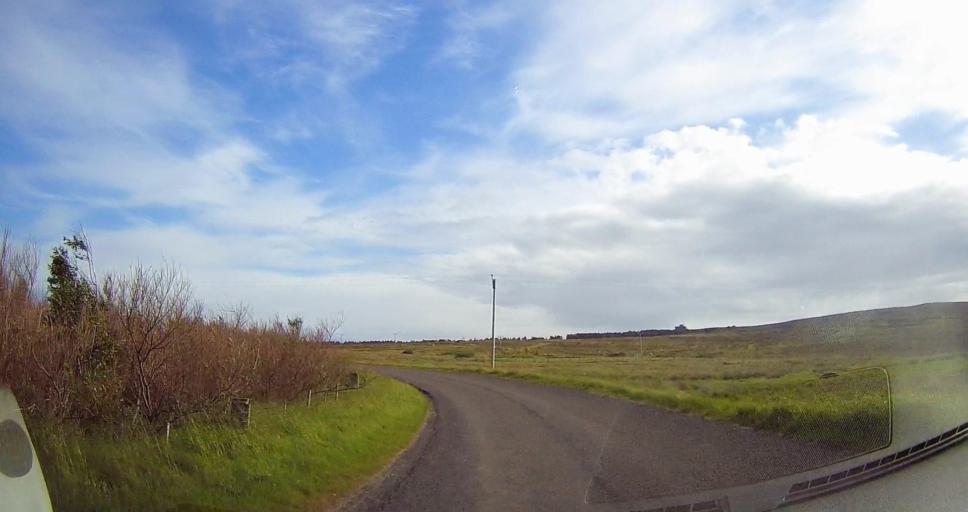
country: GB
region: Scotland
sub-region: Orkney Islands
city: Stromness
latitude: 58.8398
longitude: -3.2168
